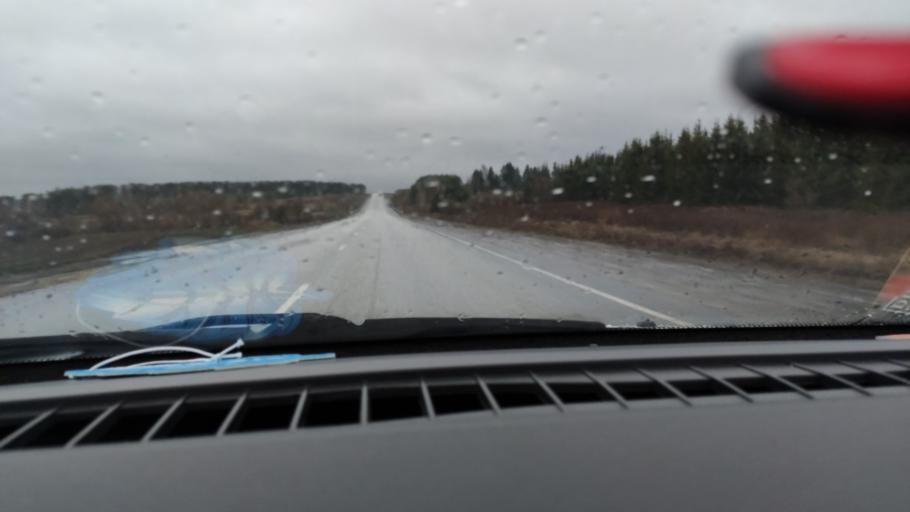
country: RU
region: Udmurtiya
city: Alnashi
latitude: 56.0580
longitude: 52.3935
